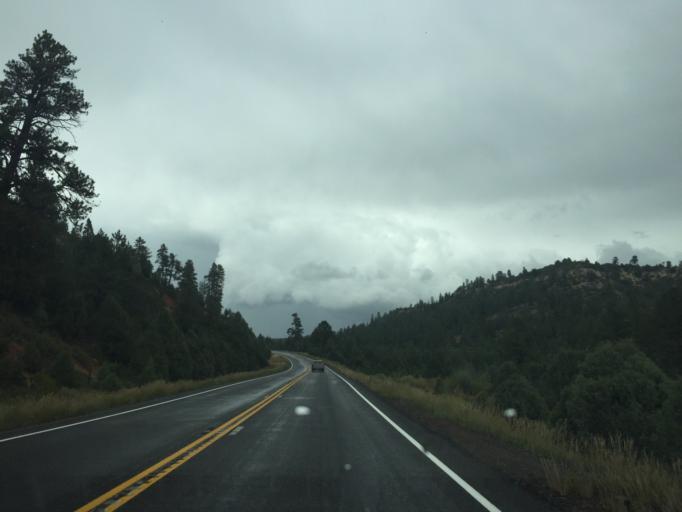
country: US
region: Utah
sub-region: Garfield County
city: Panguitch
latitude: 37.4513
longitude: -112.5302
